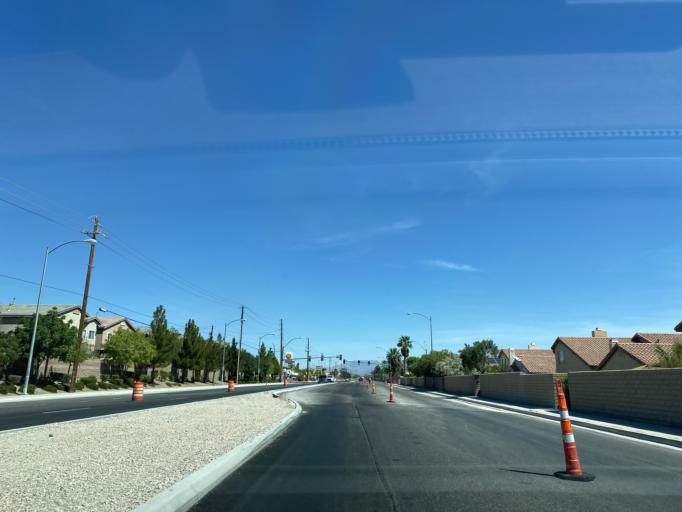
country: US
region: Nevada
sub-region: Clark County
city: Spring Valley
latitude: 36.1056
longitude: -115.2610
